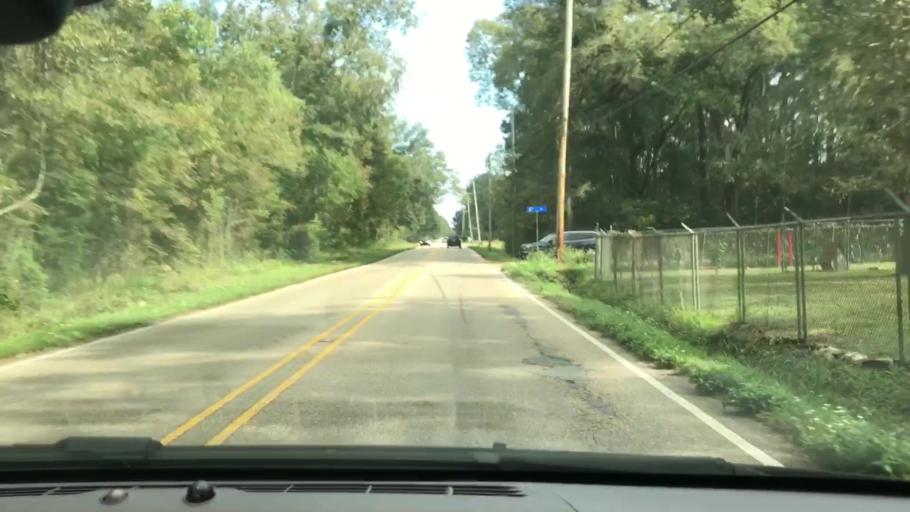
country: US
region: Louisiana
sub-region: Saint Tammany Parish
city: Abita Springs
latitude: 30.4599
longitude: -90.0625
